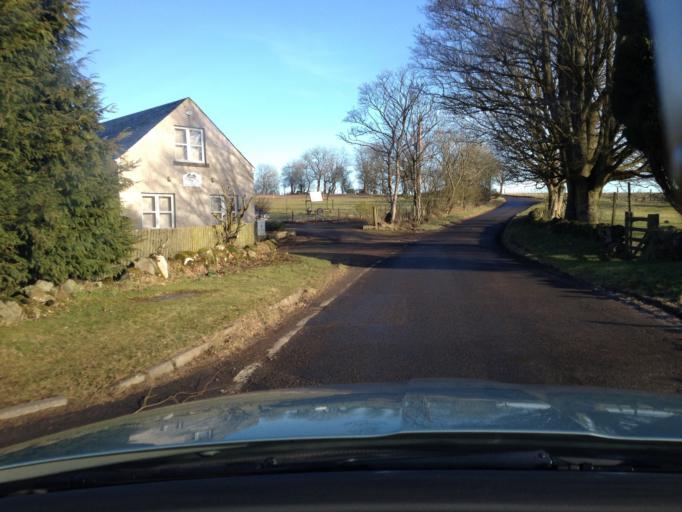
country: GB
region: Scotland
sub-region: Perth and Kinross
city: Milnathort
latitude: 56.2394
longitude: -3.4032
